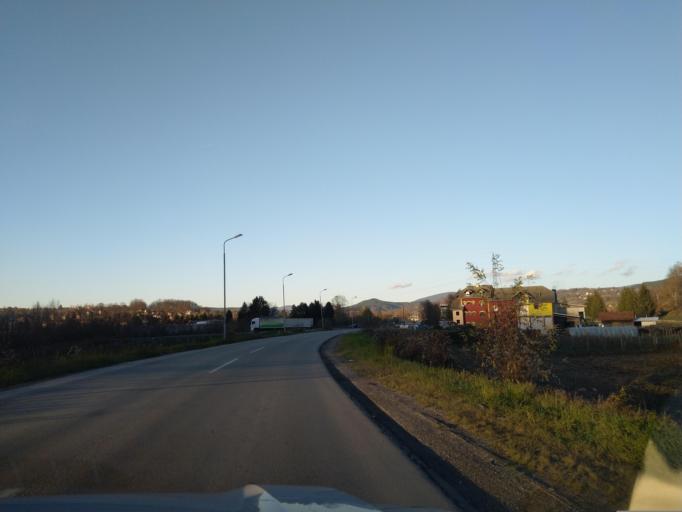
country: RS
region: Central Serbia
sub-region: Zlatiborski Okrug
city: Kosjeric
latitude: 43.9958
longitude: 19.9160
